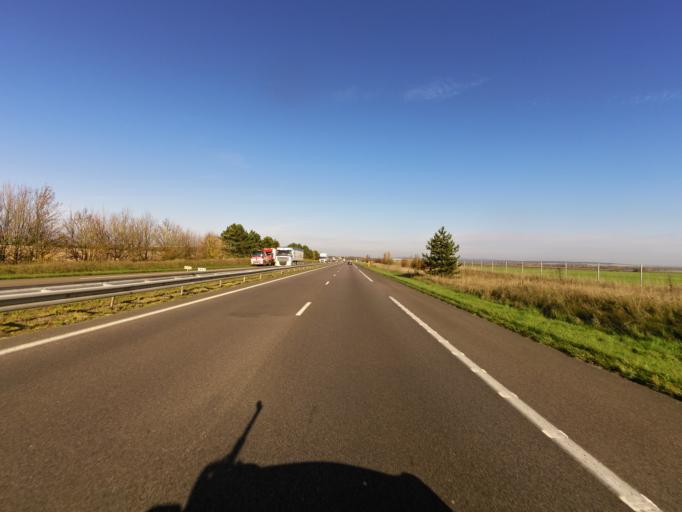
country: FR
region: Champagne-Ardenne
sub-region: Departement de la Marne
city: Verzy
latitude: 49.0990
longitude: 4.2556
